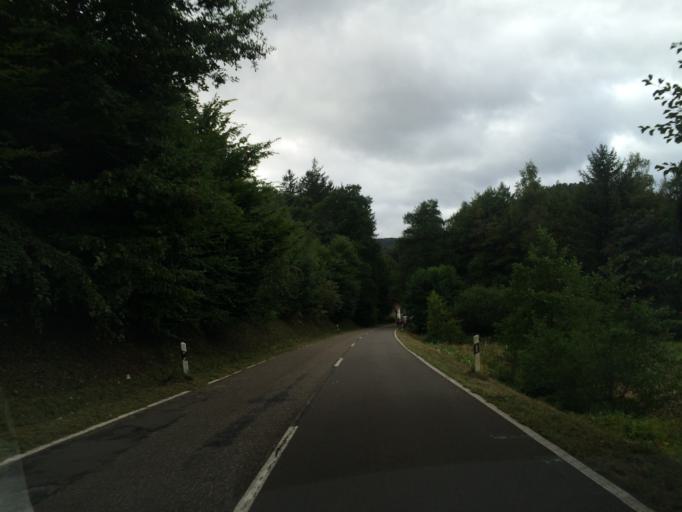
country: DE
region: Rheinland-Pfalz
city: Bobenthal
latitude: 49.0660
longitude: 7.8593
